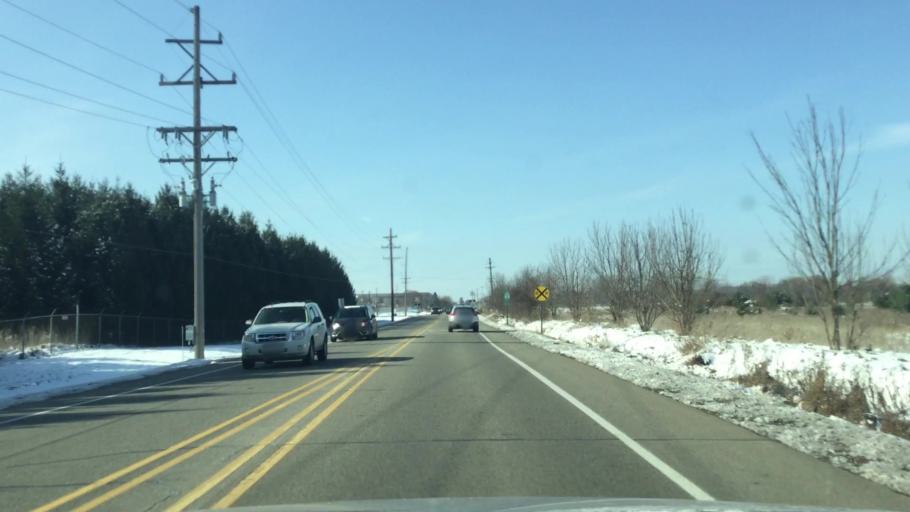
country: US
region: Michigan
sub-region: Kalamazoo County
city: Portage
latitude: 42.2157
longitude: -85.5430
